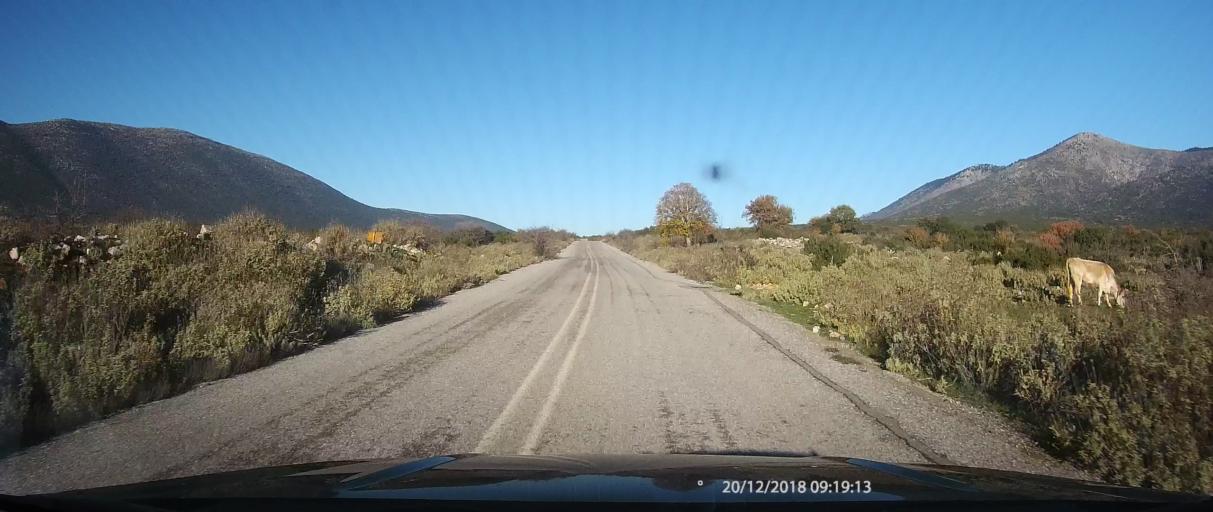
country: GR
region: Peloponnese
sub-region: Nomos Lakonias
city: Molaoi
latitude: 36.9168
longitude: 22.9437
